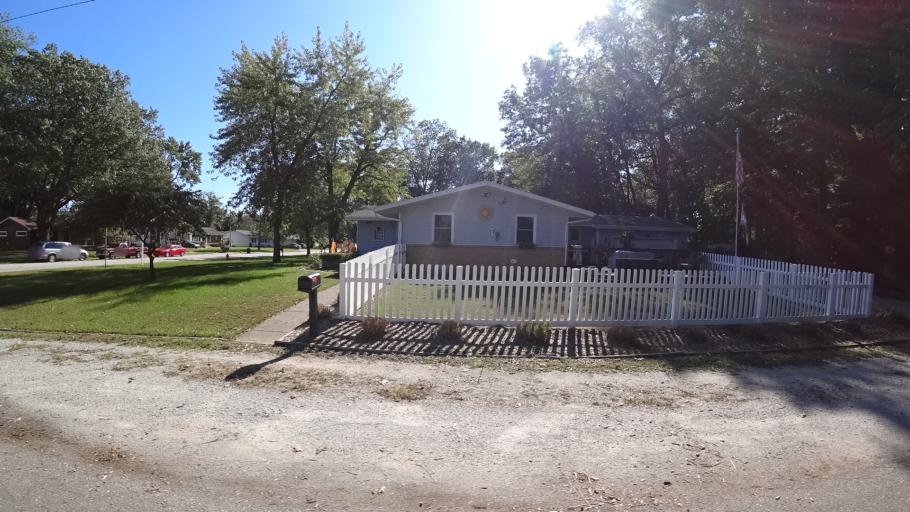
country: US
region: Indiana
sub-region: LaPorte County
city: Michigan City
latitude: 41.6934
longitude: -86.8857
